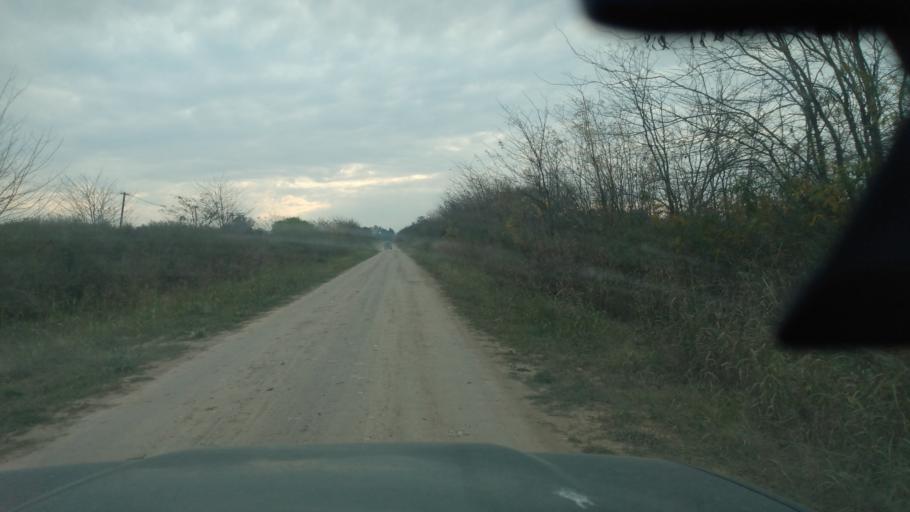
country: AR
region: Buenos Aires
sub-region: Partido de Lujan
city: Lujan
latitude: -34.5676
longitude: -59.1503
